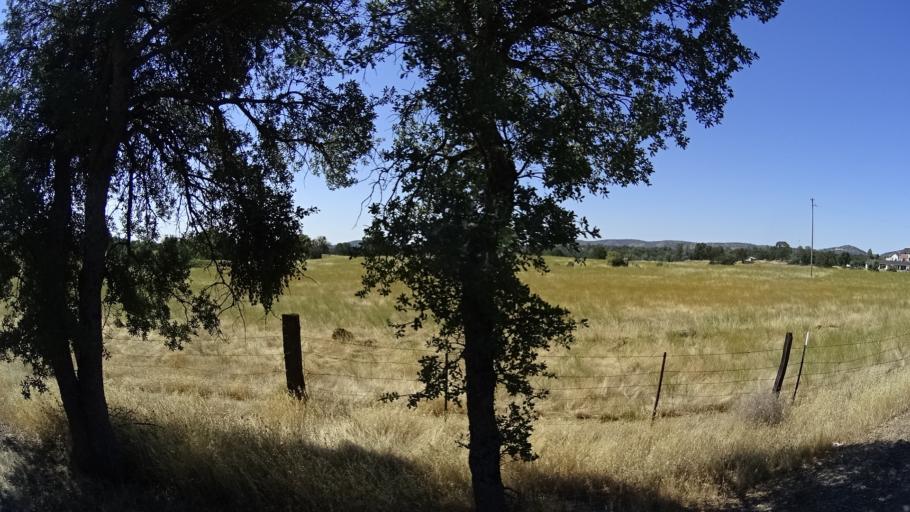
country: US
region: California
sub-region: Calaveras County
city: Copperopolis
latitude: 37.9738
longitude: -120.6485
